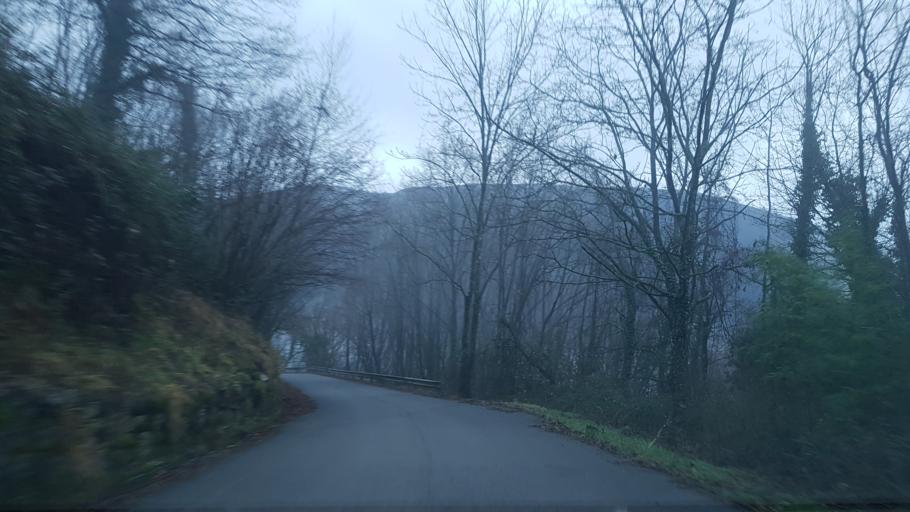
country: IT
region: Friuli Venezia Giulia
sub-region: Provincia di Udine
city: San Leonardo
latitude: 46.0884
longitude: 13.5498
